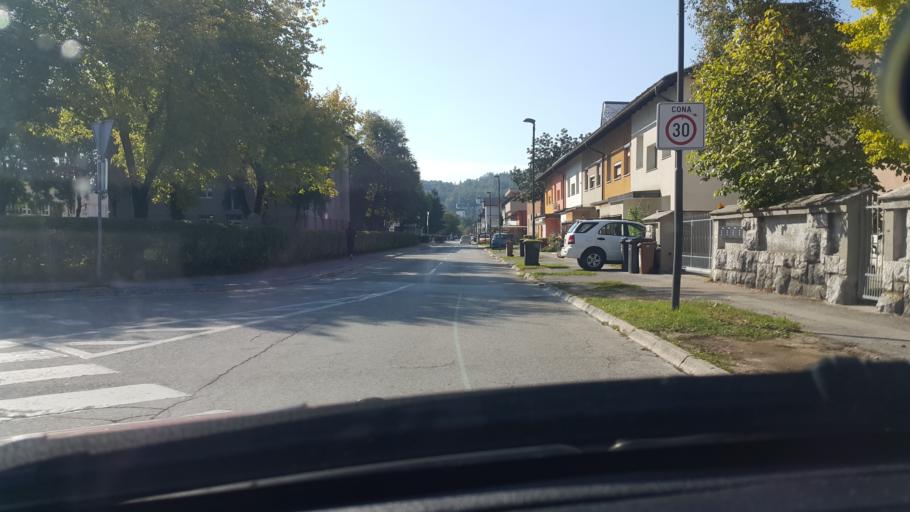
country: SI
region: Ljubljana
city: Ljubljana
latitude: 46.0709
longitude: 14.4961
